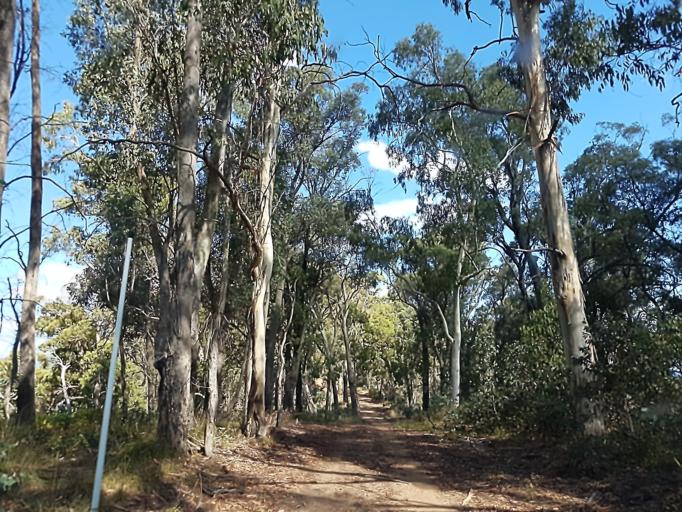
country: AU
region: Victoria
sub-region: Alpine
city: Mount Beauty
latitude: -36.8847
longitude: 147.0241
